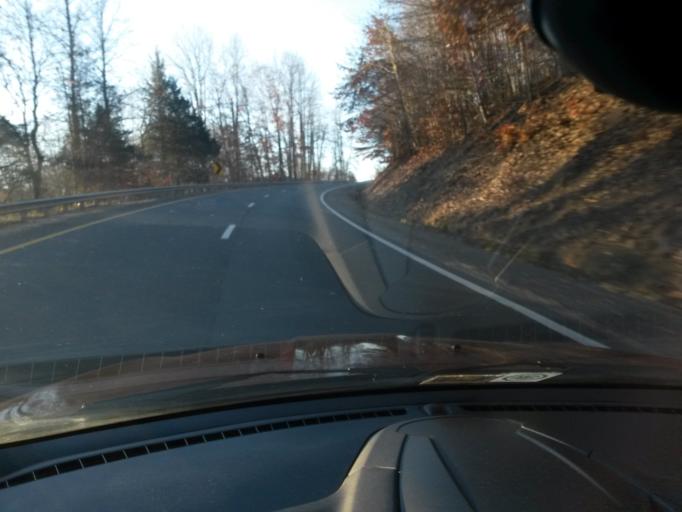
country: US
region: Virginia
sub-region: Franklin County
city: Henry Fork
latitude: 36.8779
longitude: -79.8703
